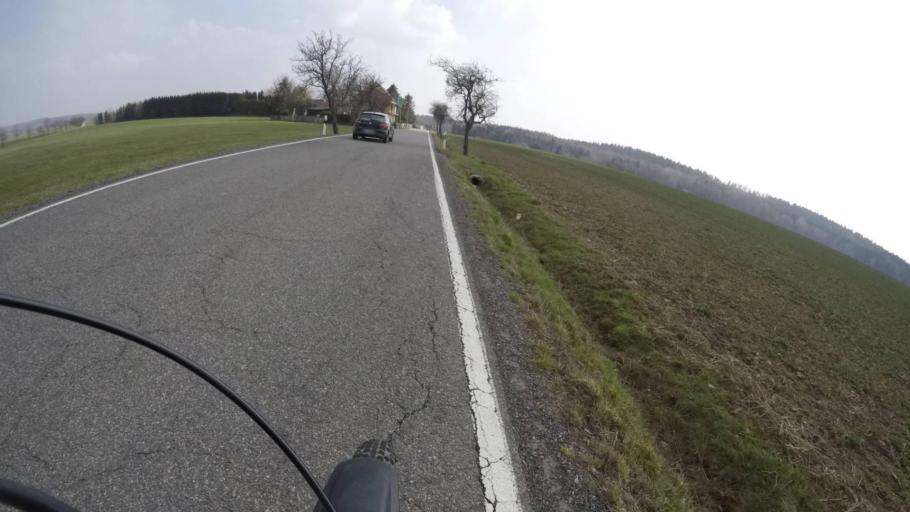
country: DE
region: Saxony
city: Limbach-Oberfrohna
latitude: 50.8332
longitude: 12.7355
